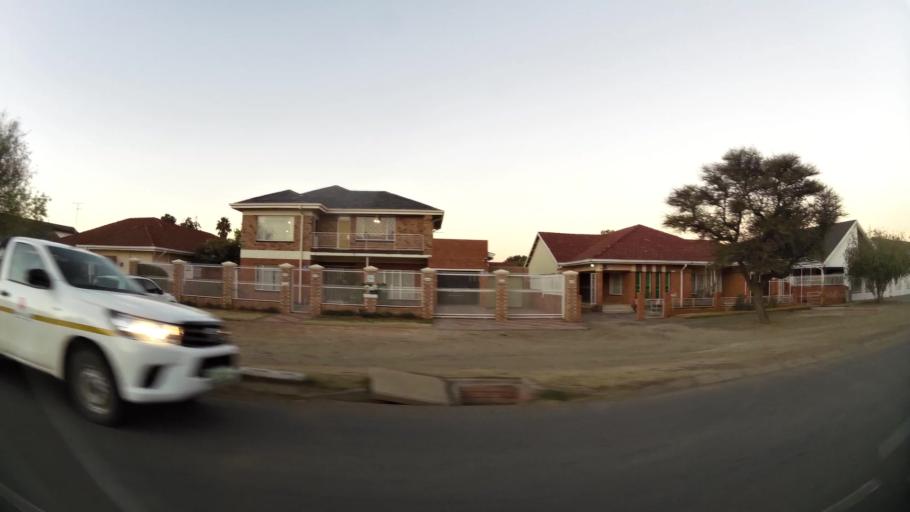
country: ZA
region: Northern Cape
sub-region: Frances Baard District Municipality
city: Kimberley
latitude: -28.7216
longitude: 24.7738
